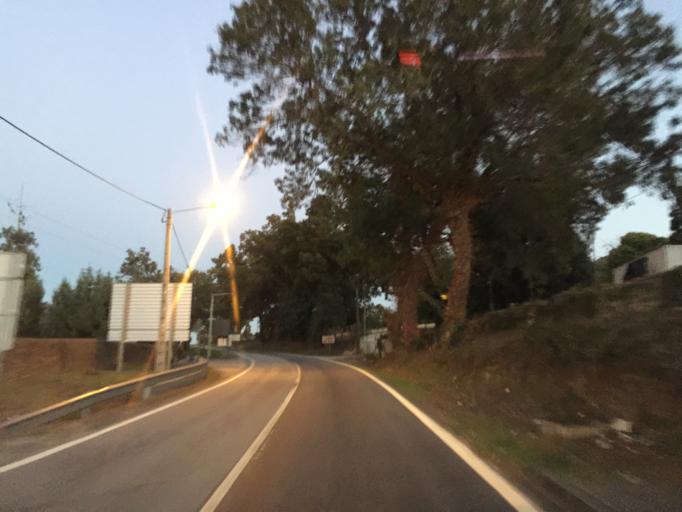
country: PT
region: Portalegre
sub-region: Castelo de Vide
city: Castelo de Vide
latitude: 39.4053
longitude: -7.4436
